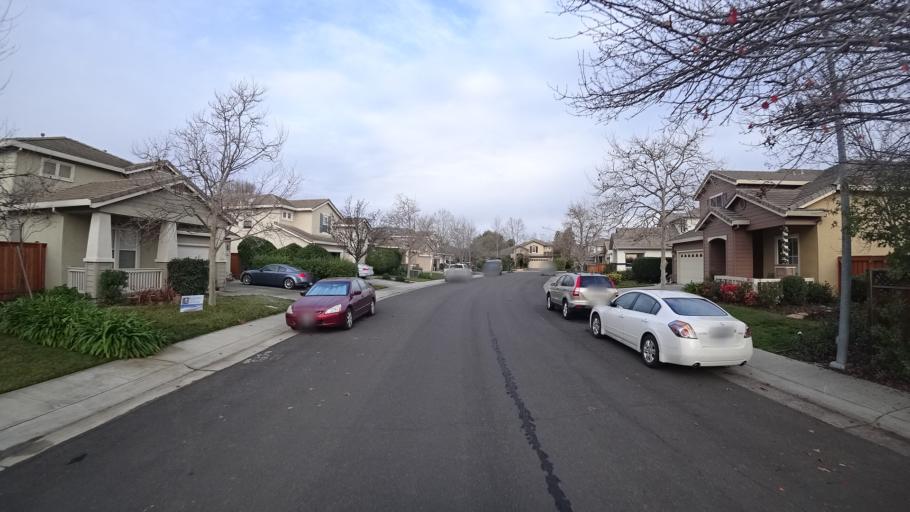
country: US
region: California
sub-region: Yolo County
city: Davis
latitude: 38.5686
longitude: -121.7160
